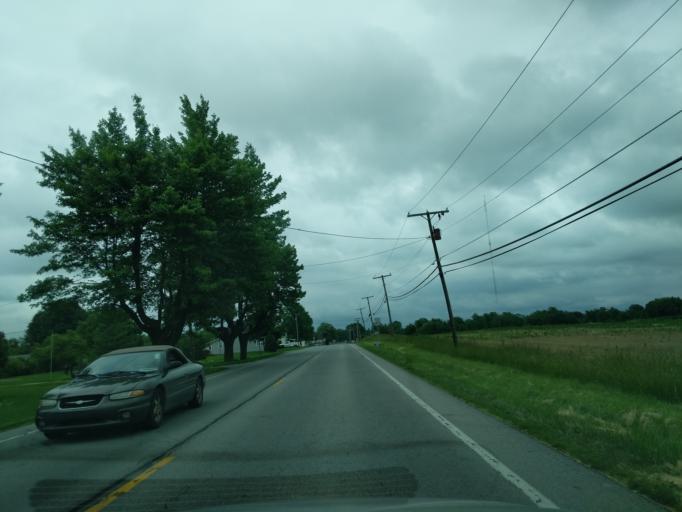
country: US
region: Indiana
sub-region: Madison County
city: Elwood
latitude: 40.2768
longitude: -85.8668
